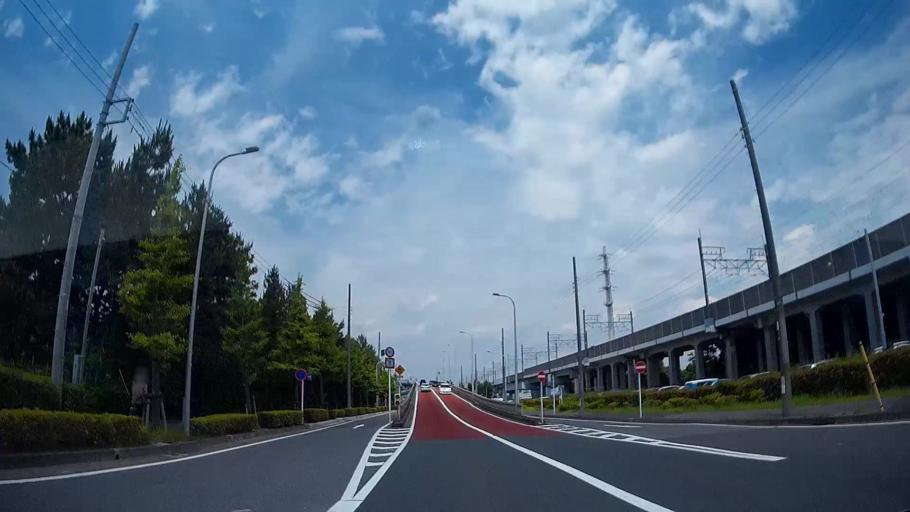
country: JP
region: Tokyo
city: Urayasu
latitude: 35.6541
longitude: 139.9169
